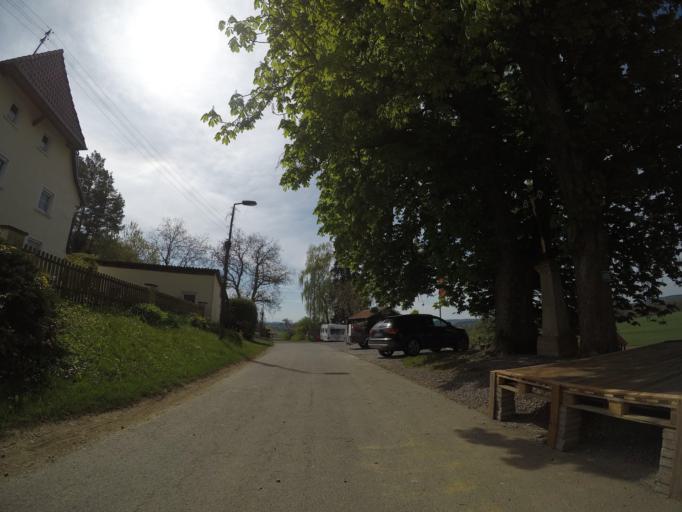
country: DE
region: Baden-Wuerttemberg
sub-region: Tuebingen Region
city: Altshausen
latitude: 47.9508
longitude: 9.5245
